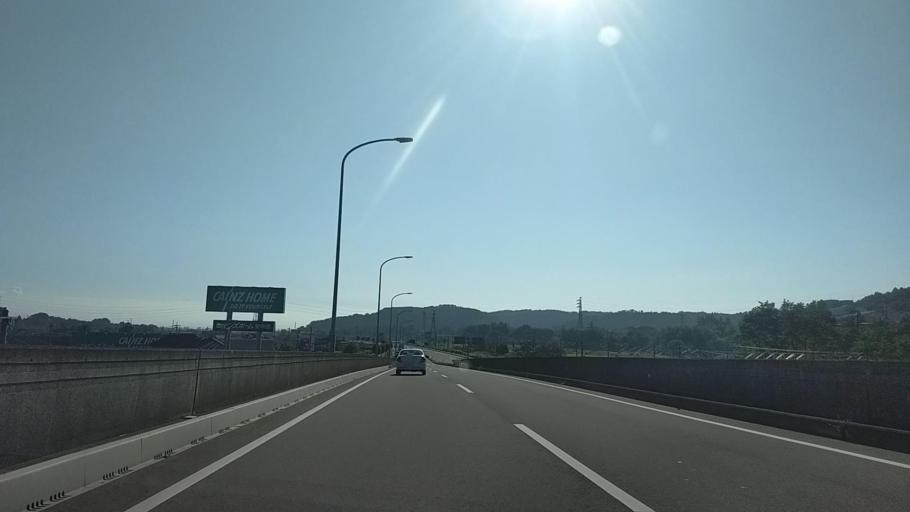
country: JP
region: Gunma
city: Annaka
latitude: 36.3324
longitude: 138.9146
